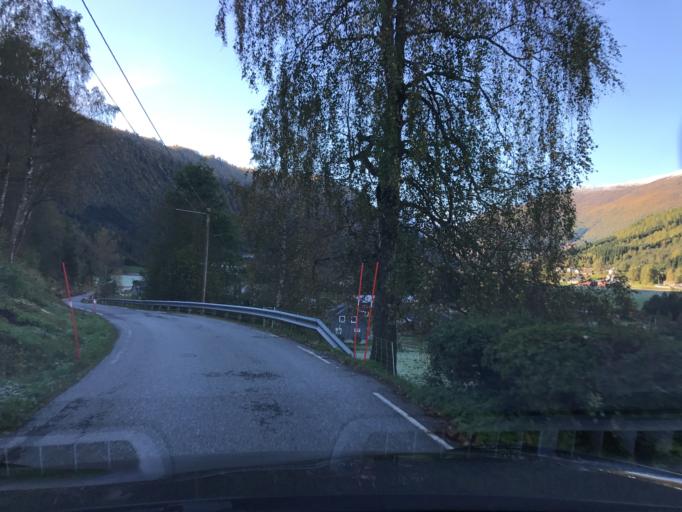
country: NO
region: More og Romsdal
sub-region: Norddal
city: Valldal
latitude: 62.3255
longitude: 7.3324
